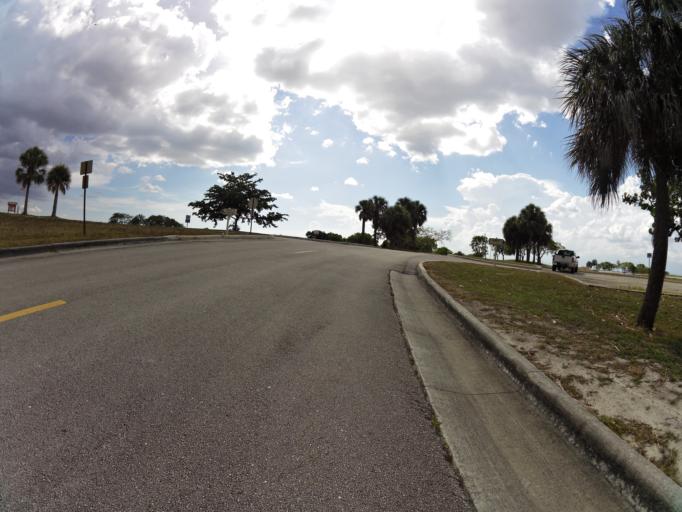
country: US
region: Florida
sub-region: Broward County
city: Southwest Ranches
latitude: 26.0674
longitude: -80.3424
